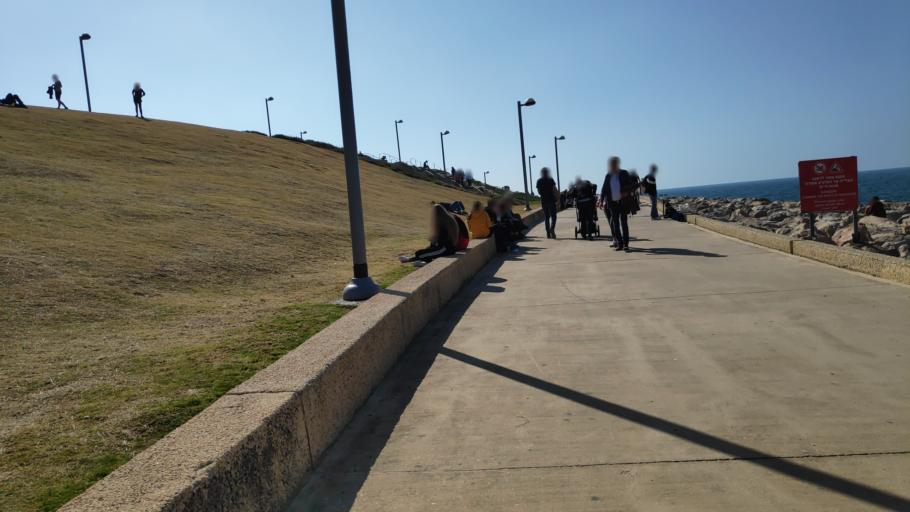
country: IL
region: Tel Aviv
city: Yafo
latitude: 32.0481
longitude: 34.7468
